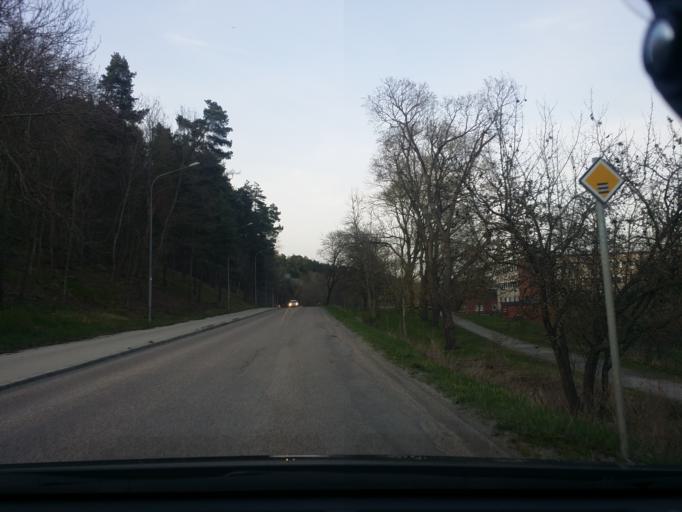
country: SE
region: Uppsala
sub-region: Enkopings Kommun
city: Enkoping
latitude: 59.6377
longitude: 17.0833
